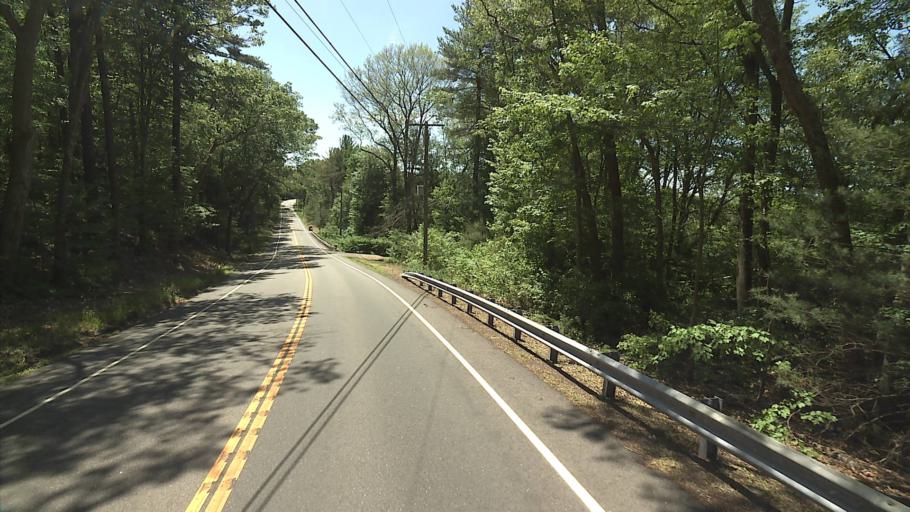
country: US
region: Rhode Island
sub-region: Washington County
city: Hopkinton
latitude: 41.5349
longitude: -71.8387
